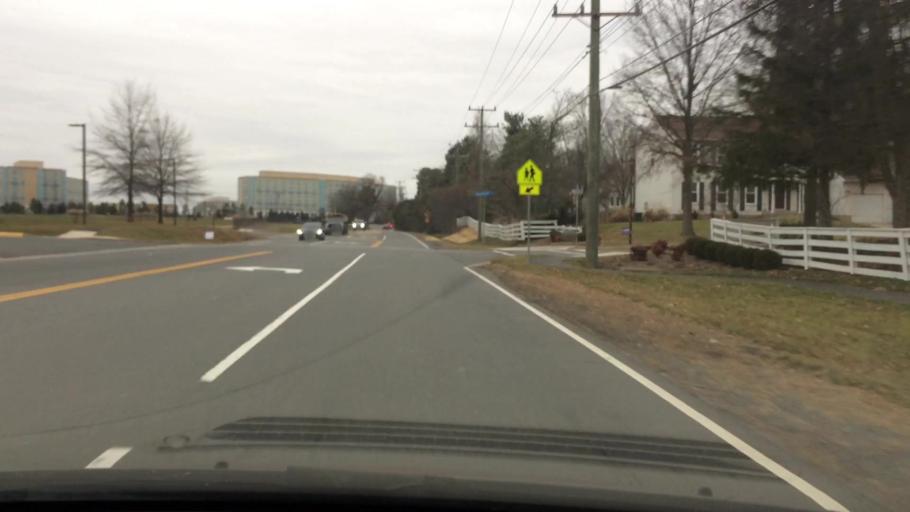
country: US
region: Virginia
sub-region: Fairfax County
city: Chantilly
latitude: 38.9077
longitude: -77.4191
